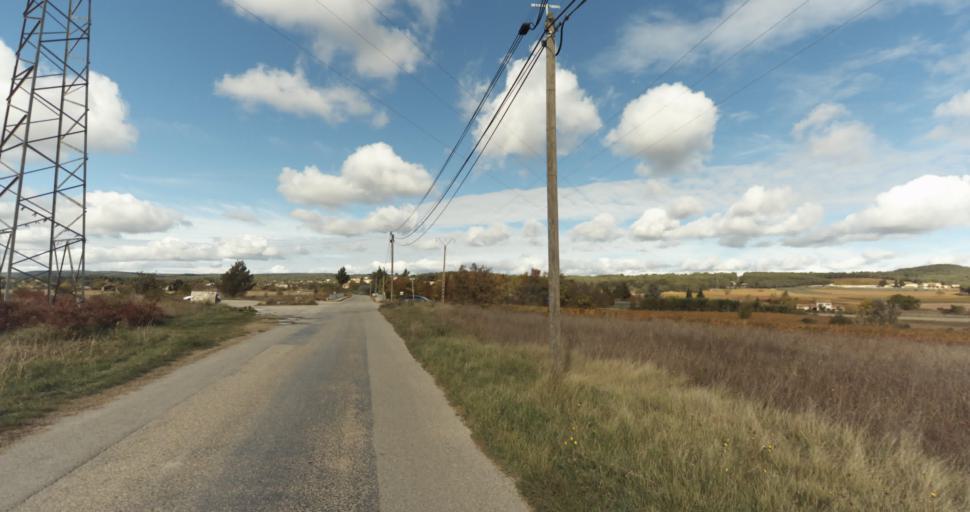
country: FR
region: Provence-Alpes-Cote d'Azur
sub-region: Departement des Bouches-du-Rhone
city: Venelles
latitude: 43.5826
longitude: 5.4937
